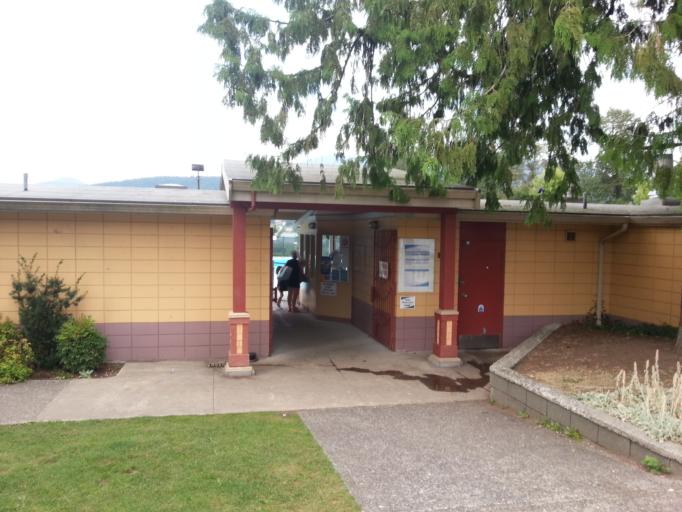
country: CA
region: British Columbia
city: Port Moody
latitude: 49.2794
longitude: -122.8492
